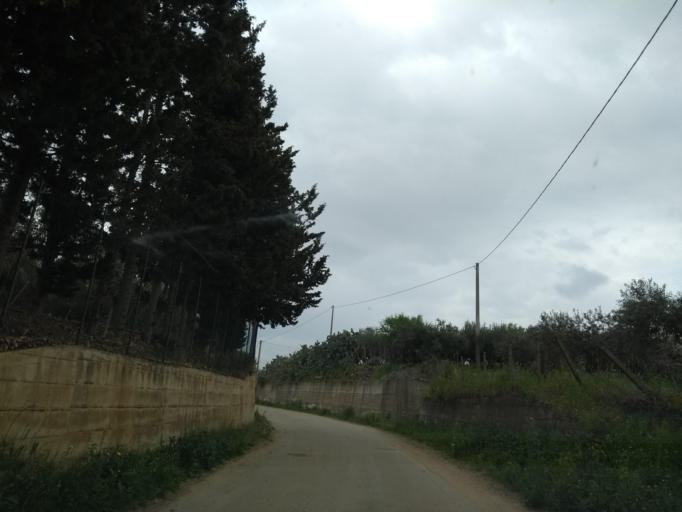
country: IT
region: Sicily
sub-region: Palermo
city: Partinico
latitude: 37.9922
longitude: 13.0742
